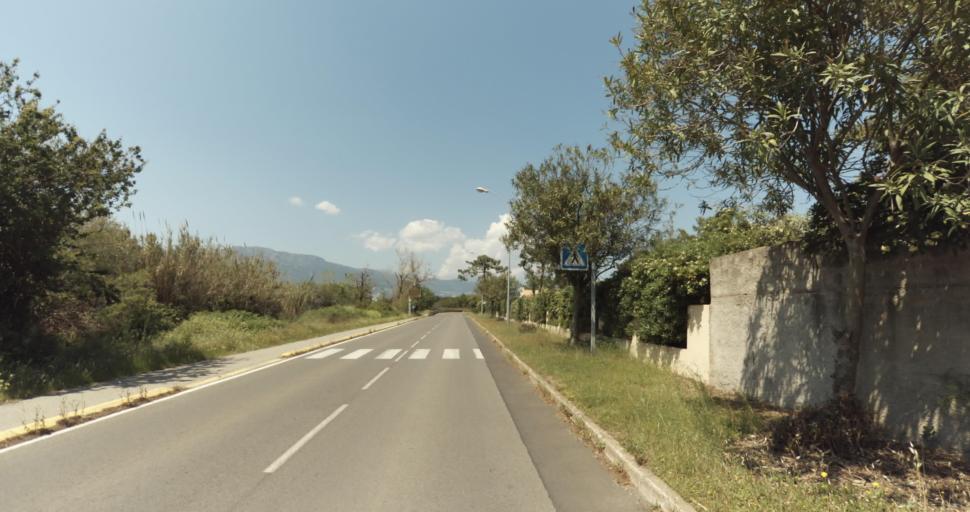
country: FR
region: Corsica
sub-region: Departement de la Haute-Corse
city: Biguglia
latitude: 42.6388
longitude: 9.4595
